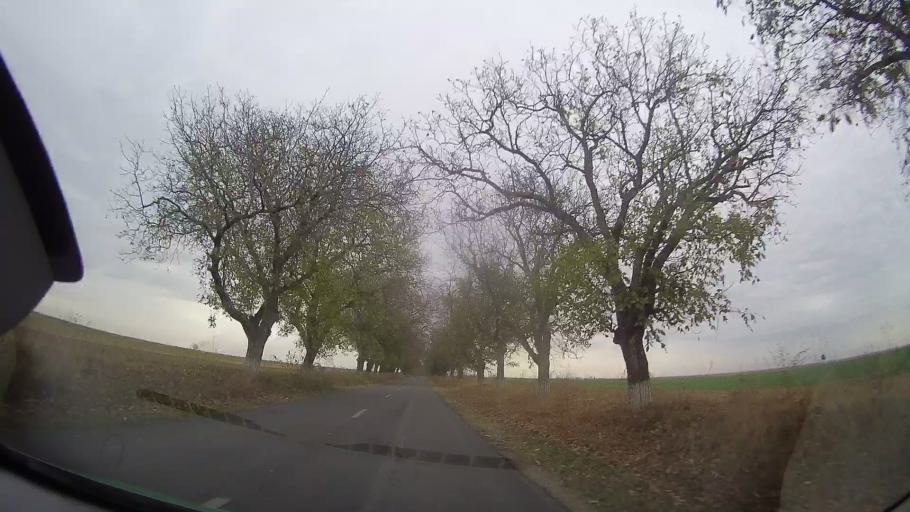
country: RO
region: Prahova
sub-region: Comuna Fantanele
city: Fantanele
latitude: 45.0182
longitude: 26.3981
